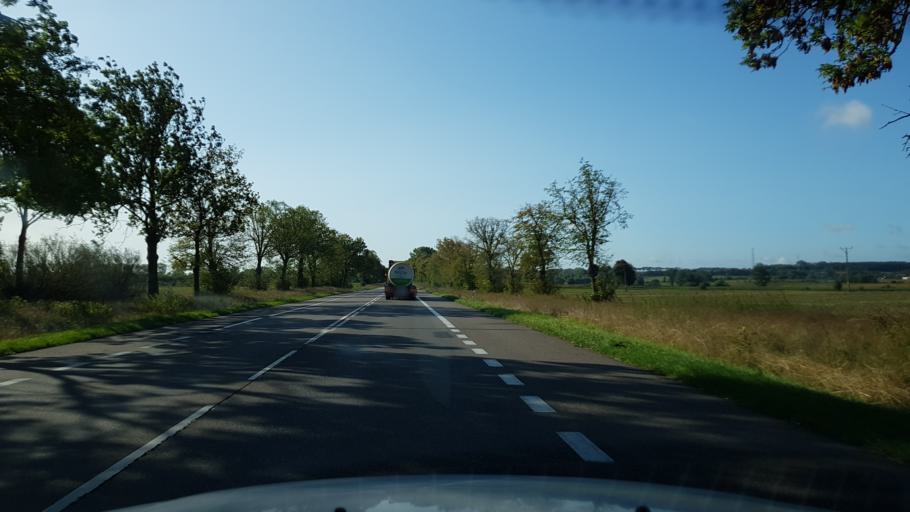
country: PL
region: West Pomeranian Voivodeship
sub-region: Powiat pyrzycki
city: Pyrzyce
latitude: 53.0864
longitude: 14.9006
